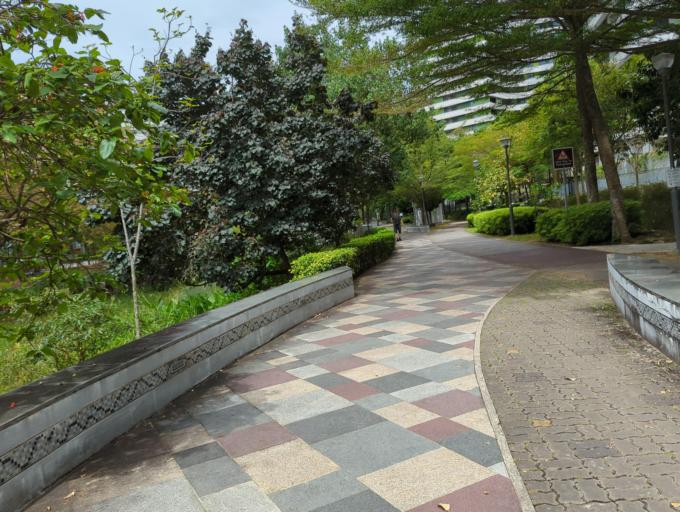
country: MY
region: Johor
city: Kampung Pasir Gudang Baru
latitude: 1.4086
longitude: 103.9009
